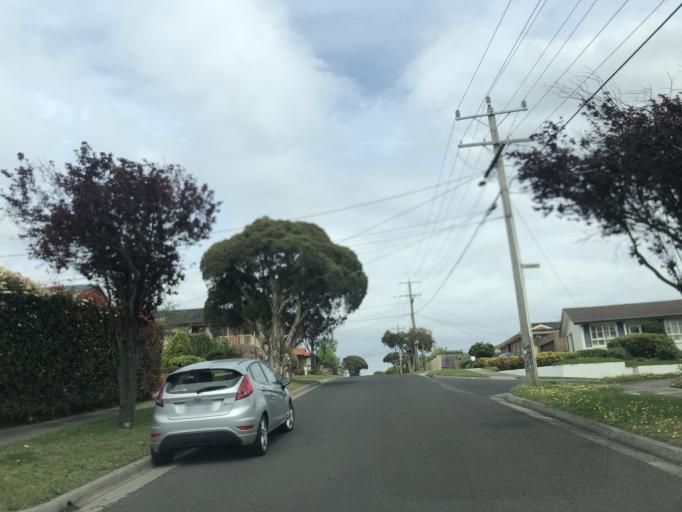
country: AU
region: Victoria
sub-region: Greater Dandenong
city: Noble Park North
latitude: -37.9425
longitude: 145.2122
